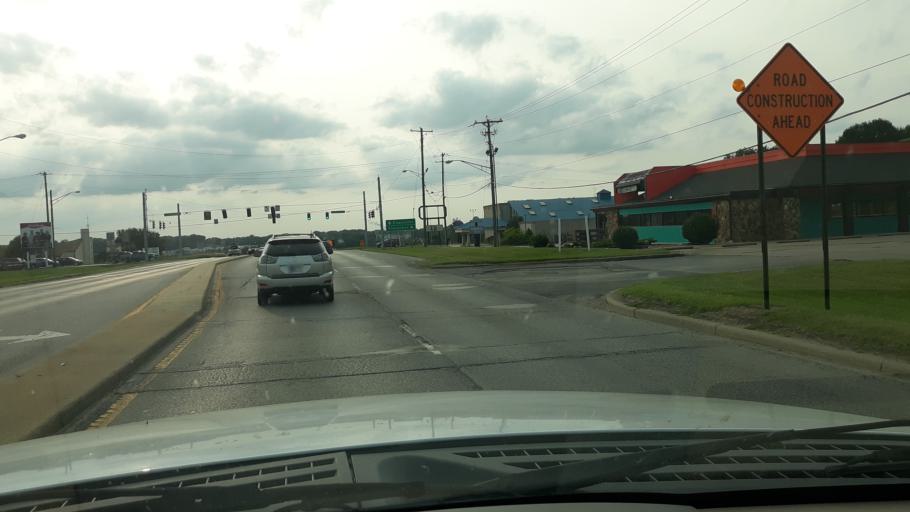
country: US
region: Indiana
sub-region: Gibson County
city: Princeton
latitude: 38.3555
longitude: -87.5920
